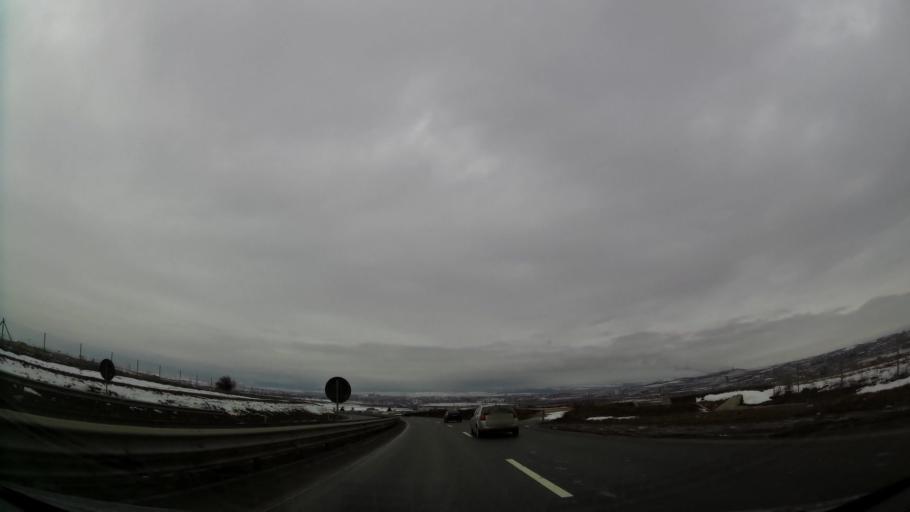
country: XK
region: Pristina
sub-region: Komuna e Prishtines
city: Pristina
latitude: 42.6320
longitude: 21.1424
